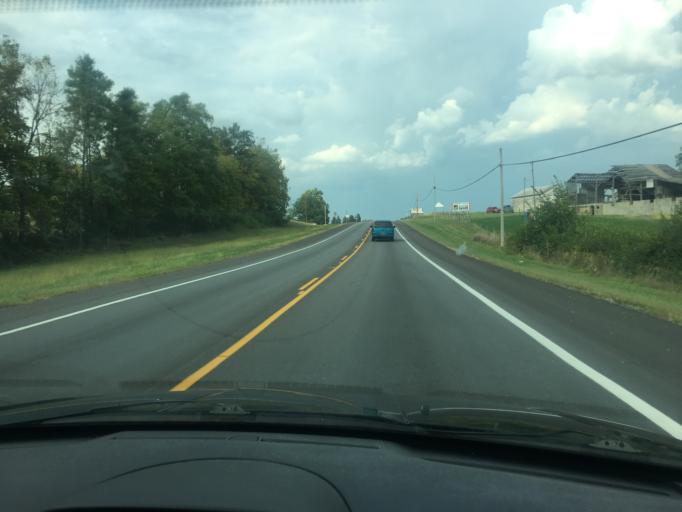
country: US
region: Ohio
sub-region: Champaign County
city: Urbana
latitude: 40.0766
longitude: -83.7649
